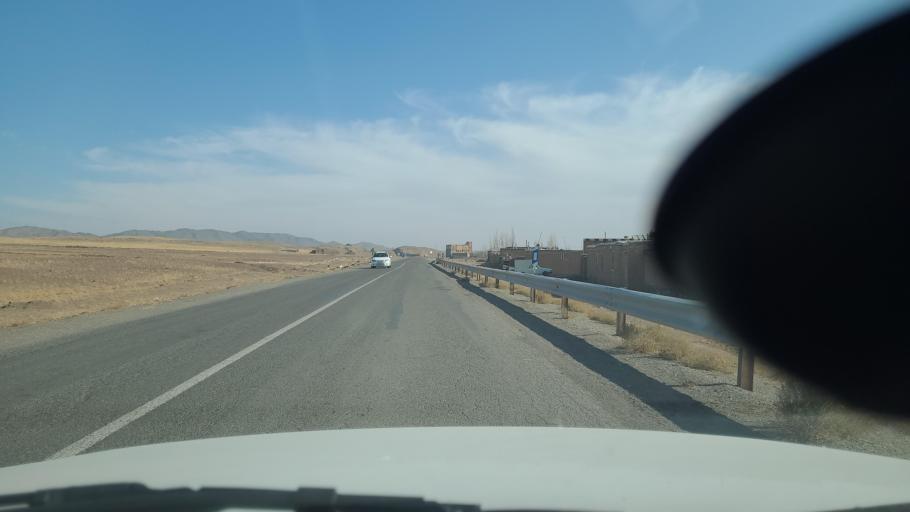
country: IR
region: Razavi Khorasan
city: Fariman
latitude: 35.5928
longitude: 59.6826
